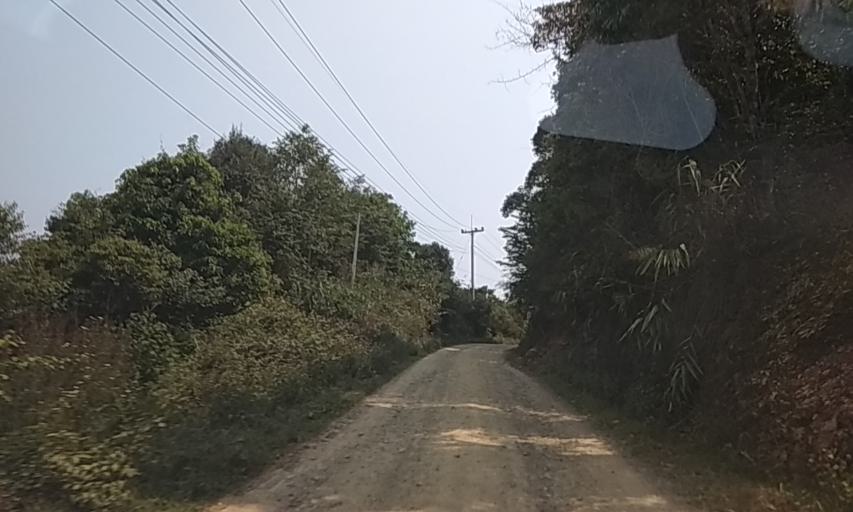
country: TH
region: Nan
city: Chaloem Phra Kiat
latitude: 20.0338
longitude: 101.0921
